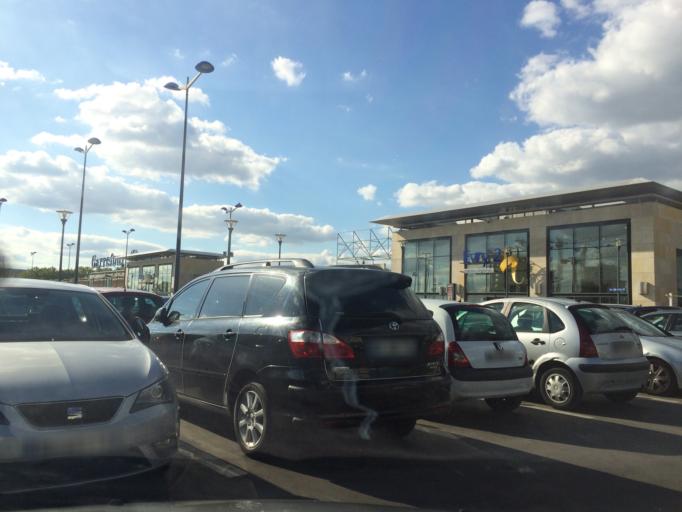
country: FR
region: Ile-de-France
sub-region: Departement de l'Essonne
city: Evry
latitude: 48.6272
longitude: 2.4277
